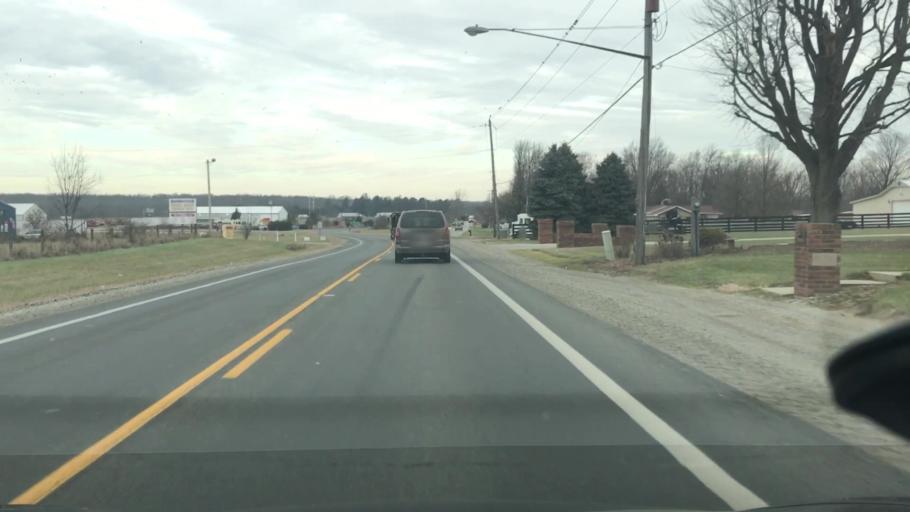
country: US
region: Ohio
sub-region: Madison County
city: Choctaw Lake
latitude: 39.9382
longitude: -83.4952
